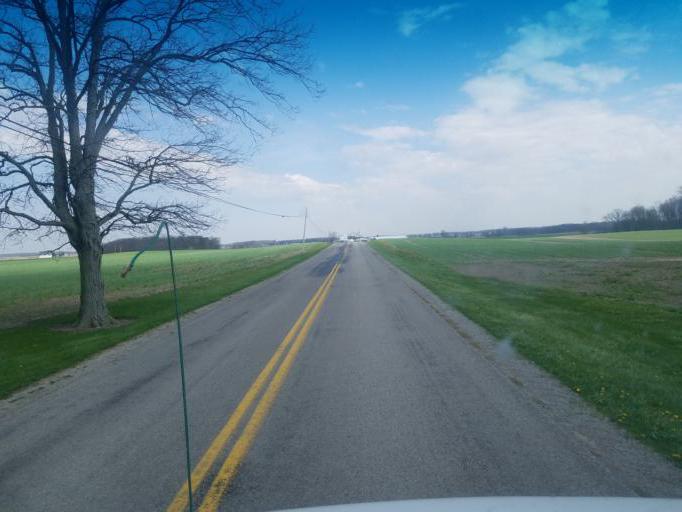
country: US
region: Ohio
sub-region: Hardin County
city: Kenton
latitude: 40.6118
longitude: -83.6694
